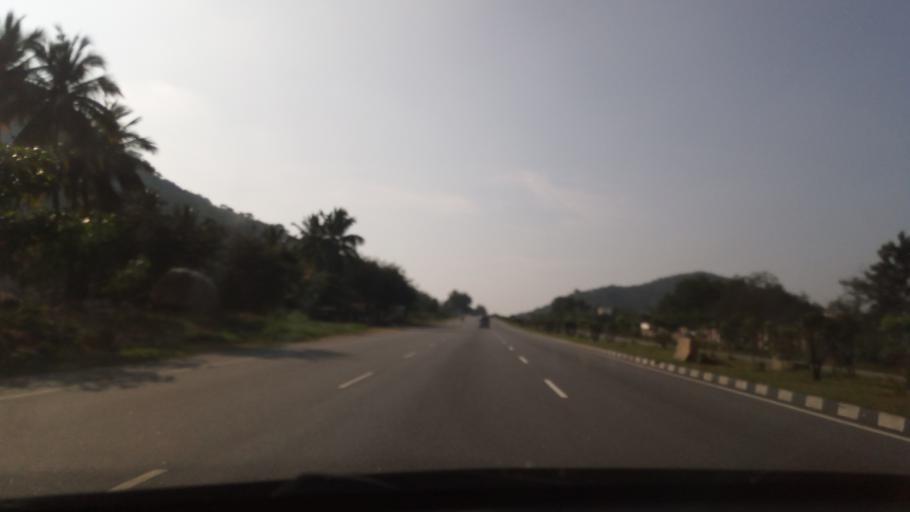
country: IN
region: Tamil Nadu
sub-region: Krishnagiri
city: Krishnagiri
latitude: 12.5360
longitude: 78.3849
